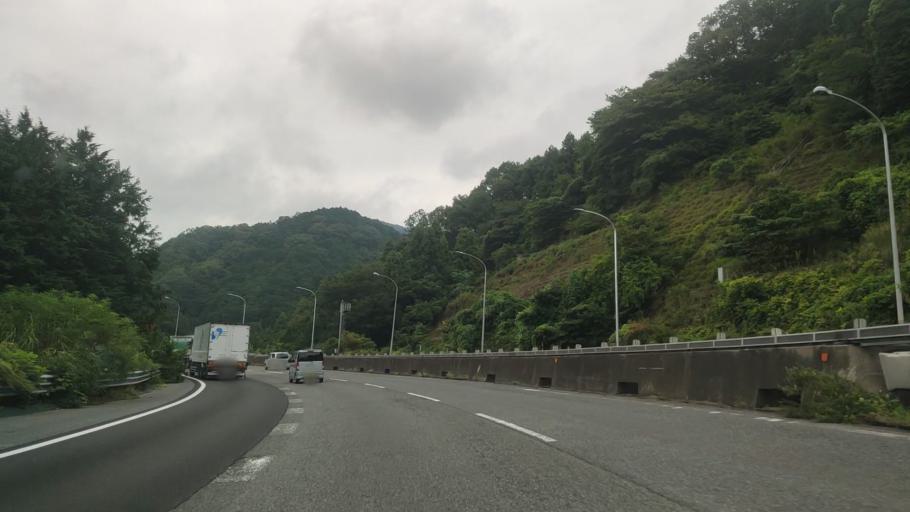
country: JP
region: Nara
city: Tenri
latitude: 34.6119
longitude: 135.8756
